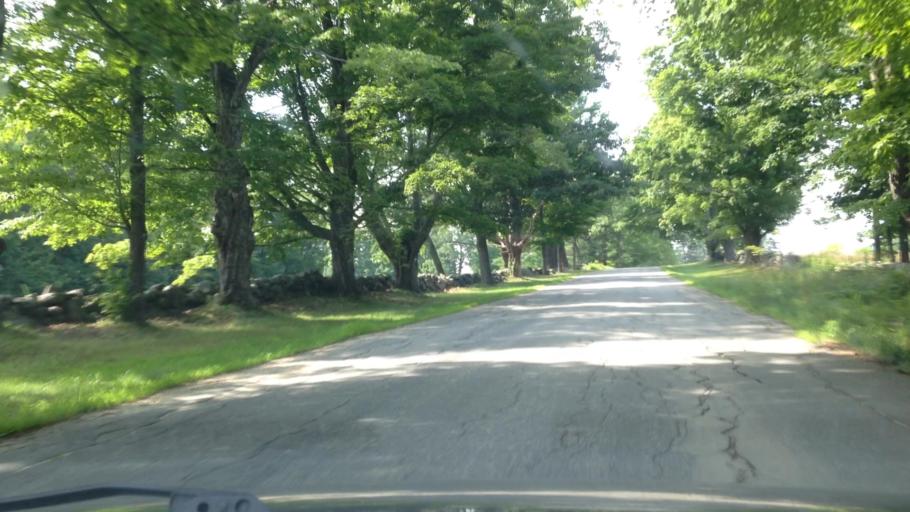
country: US
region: New Hampshire
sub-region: Cheshire County
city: Marlborough
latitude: 42.8912
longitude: -72.1932
